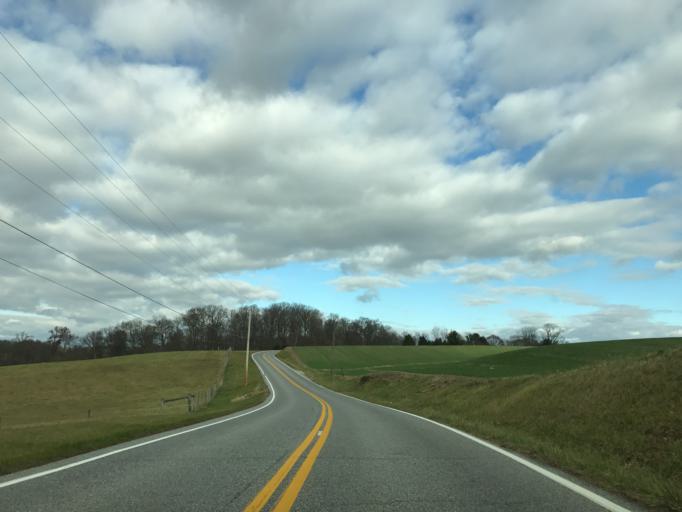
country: US
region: Pennsylvania
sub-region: York County
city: Stewartstown
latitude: 39.6535
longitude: -76.6103
